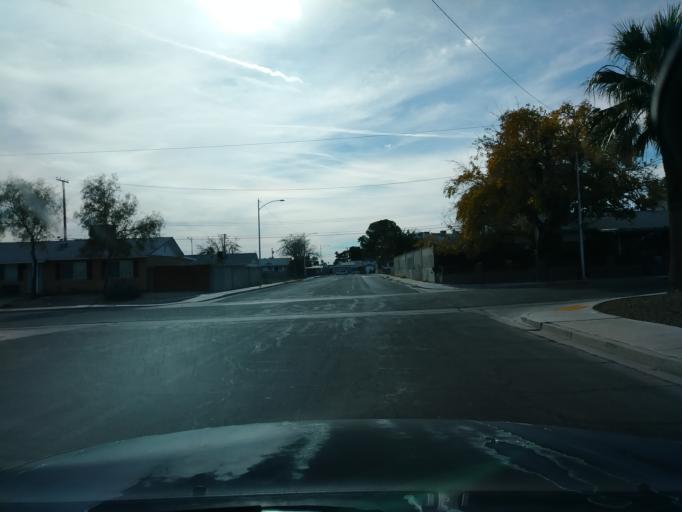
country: US
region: Nevada
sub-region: Clark County
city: Spring Valley
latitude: 36.1653
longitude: -115.2401
